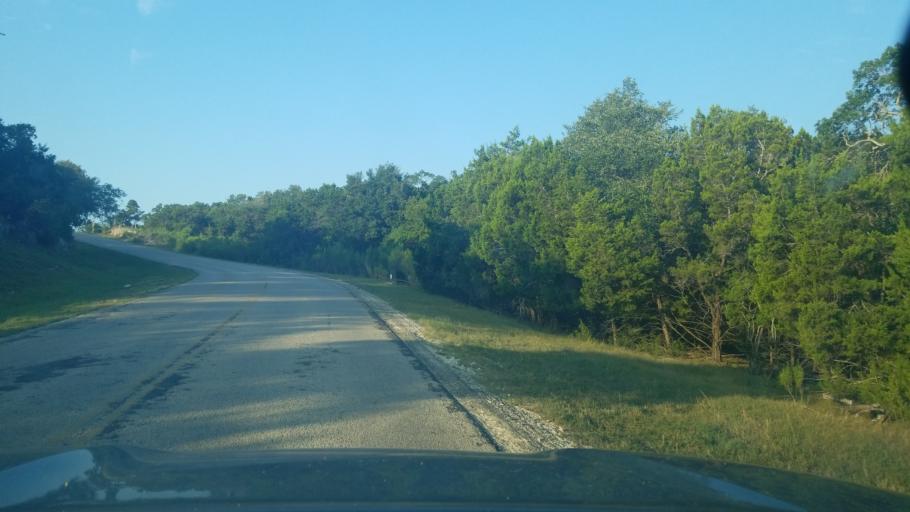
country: US
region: Texas
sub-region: Comal County
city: Bulverde
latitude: 29.8092
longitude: -98.4079
